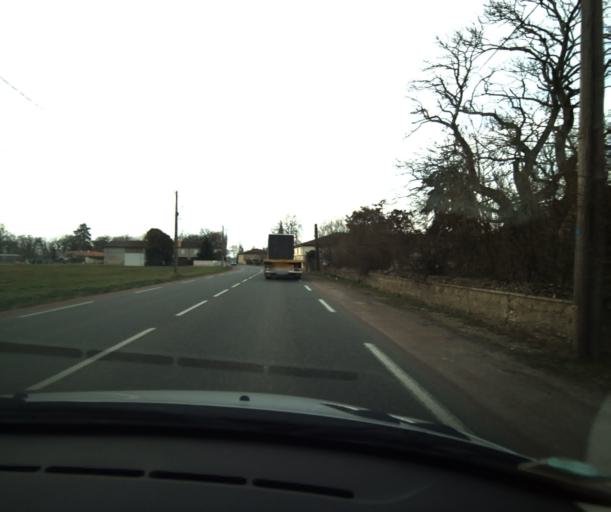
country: FR
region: Midi-Pyrenees
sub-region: Departement du Tarn-et-Garonne
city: Saint-Porquier
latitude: 44.0193
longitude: 1.1598
